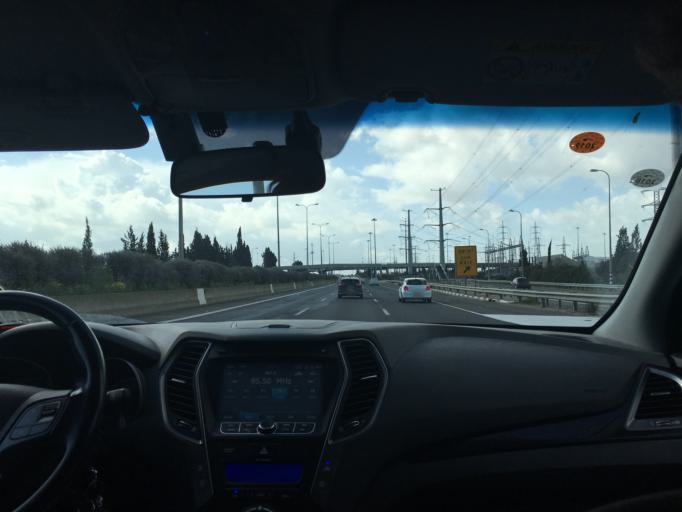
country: IL
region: Tel Aviv
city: Azor
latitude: 32.0240
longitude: 34.8252
